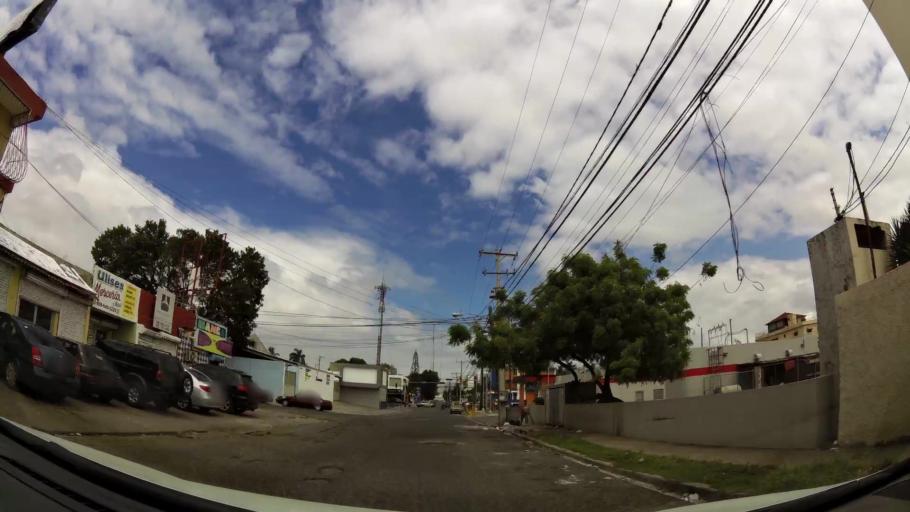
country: DO
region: Nacional
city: Bella Vista
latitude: 18.4756
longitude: -69.9540
